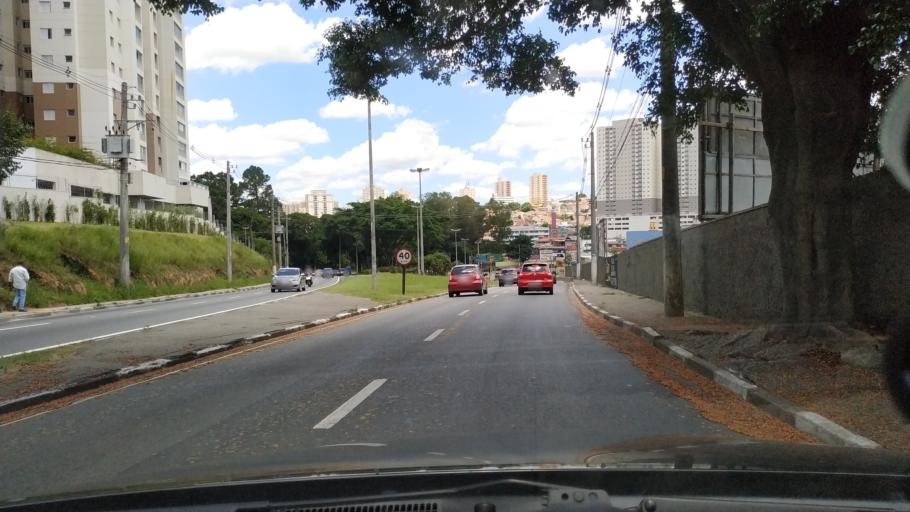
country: BR
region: Sao Paulo
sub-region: Barueri
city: Barueri
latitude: -23.4952
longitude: -46.8774
